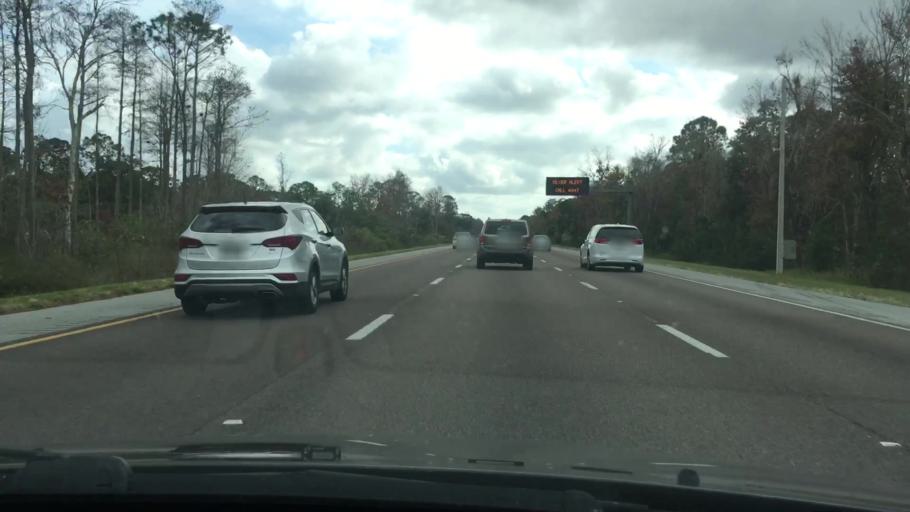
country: US
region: Florida
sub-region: Volusia County
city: Glencoe
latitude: 28.9782
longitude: -80.9656
